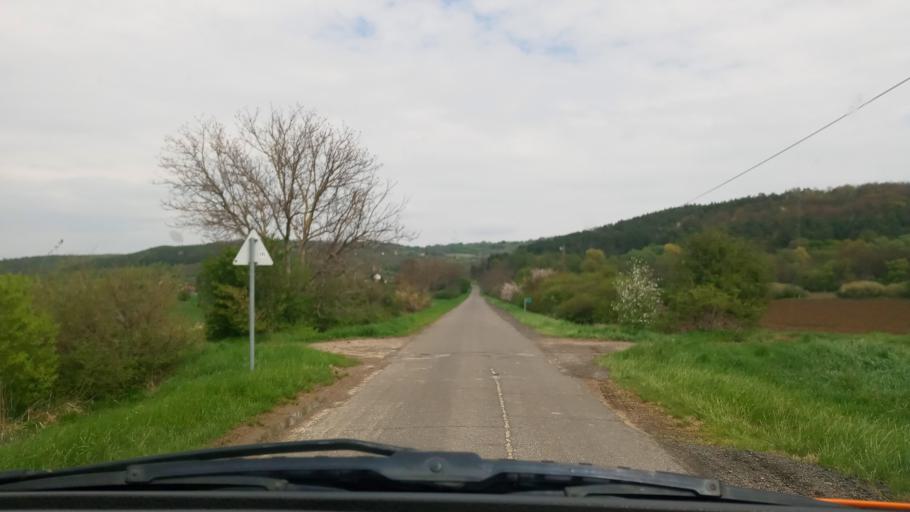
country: HU
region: Baranya
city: Sasd
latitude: 46.2601
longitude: 18.1173
